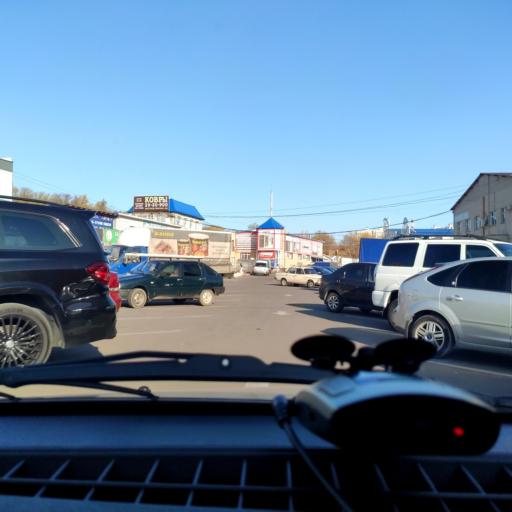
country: RU
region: Voronezj
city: Pridonskoy
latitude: 51.6715
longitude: 39.1232
